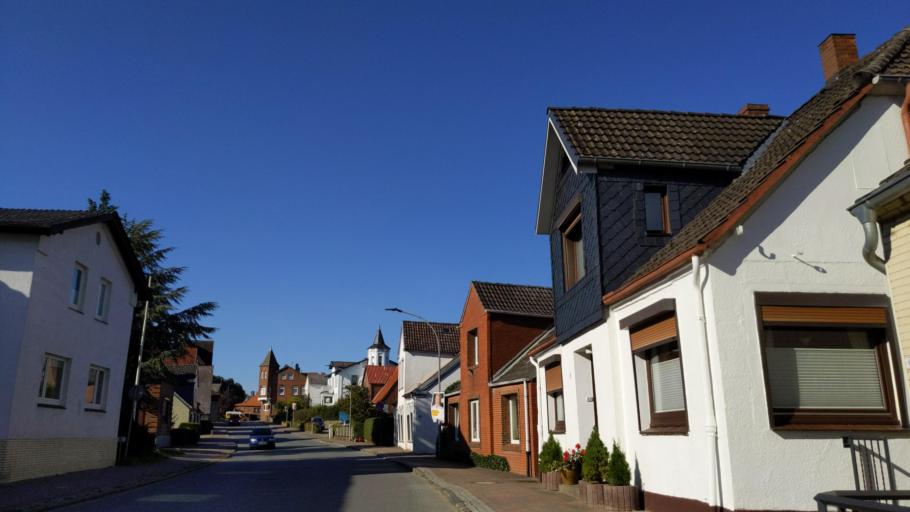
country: DE
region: Schleswig-Holstein
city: Ahrensbok
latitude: 54.0050
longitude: 10.5764
